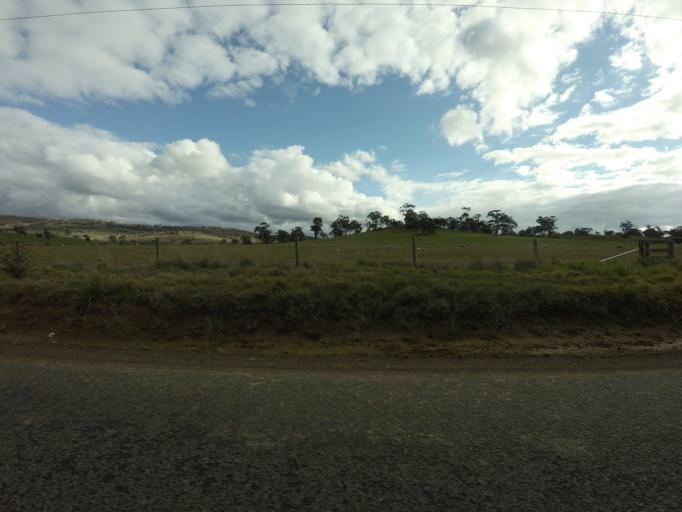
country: AU
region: Tasmania
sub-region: Northern Midlands
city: Evandale
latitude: -41.8805
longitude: 147.3072
